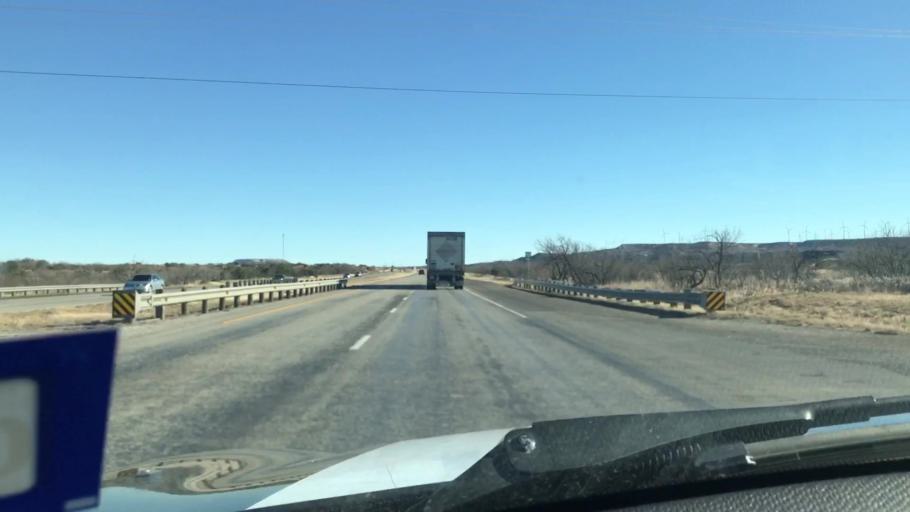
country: US
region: Texas
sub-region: Garza County
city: Post
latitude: 32.9958
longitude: -101.1510
